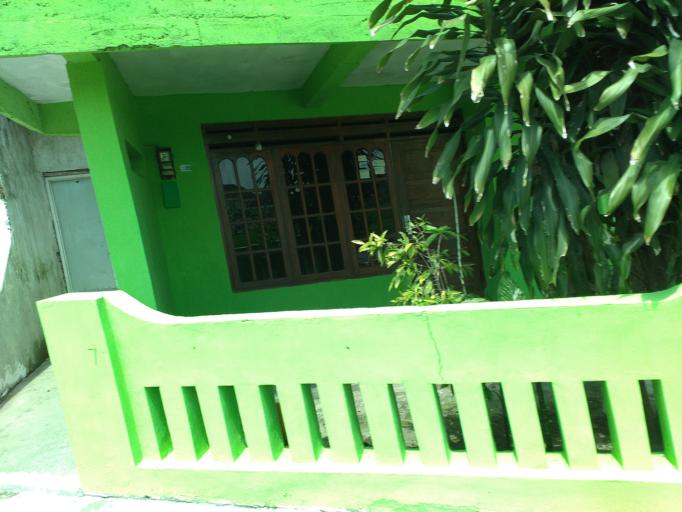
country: ID
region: Central Java
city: Klaten
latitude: -7.7031
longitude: 110.5933
